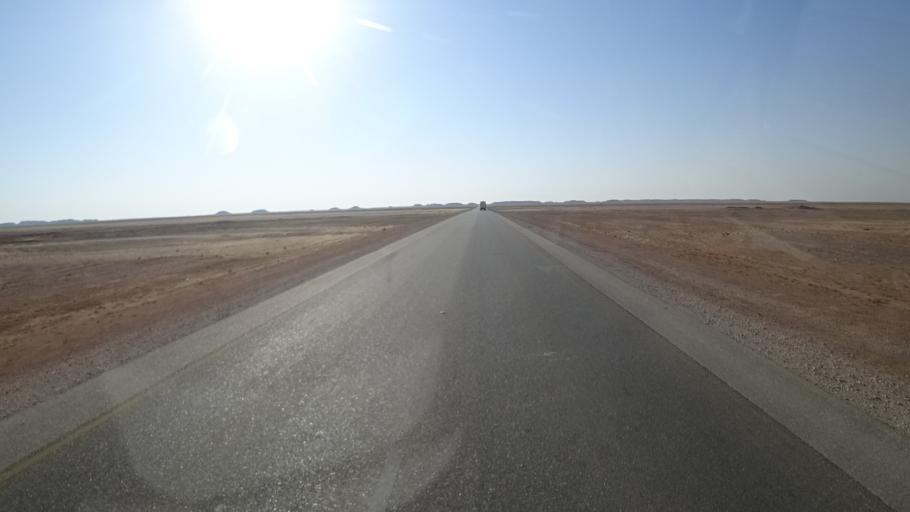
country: OM
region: Zufar
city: Salalah
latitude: 17.6426
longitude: 53.8414
